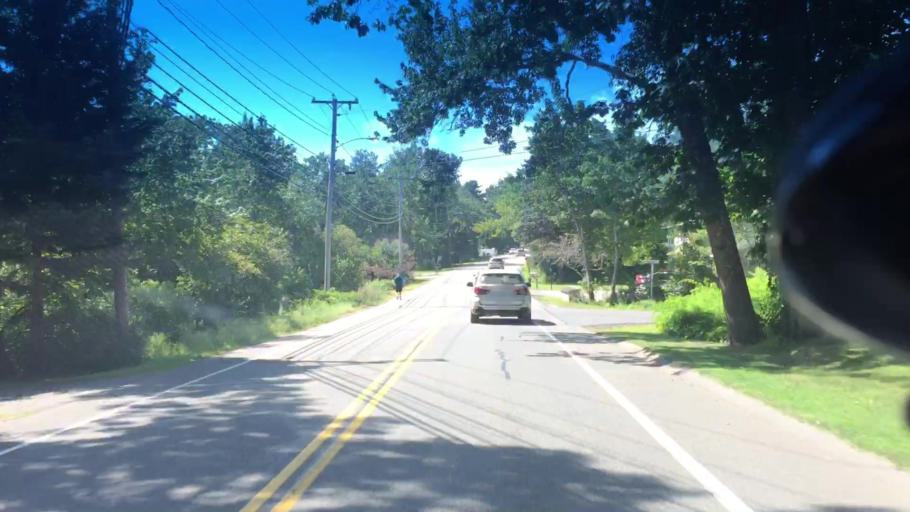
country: US
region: Maine
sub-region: York County
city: York Beach
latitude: 43.1693
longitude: -70.6204
